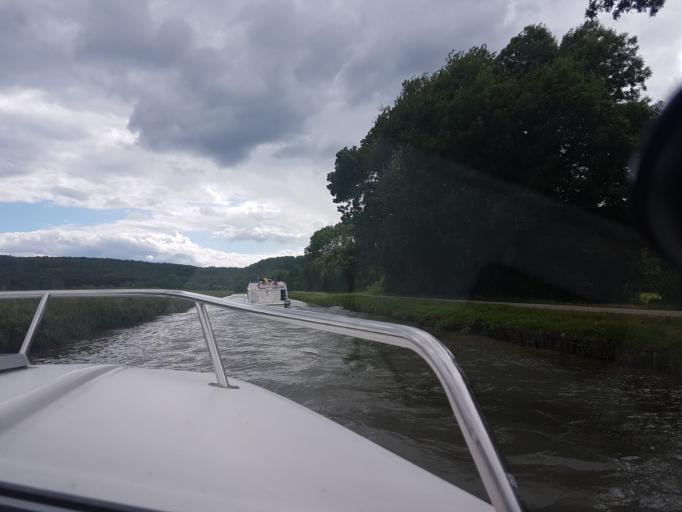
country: FR
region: Bourgogne
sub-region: Departement de l'Yonne
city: Vermenton
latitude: 47.5723
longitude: 3.6416
